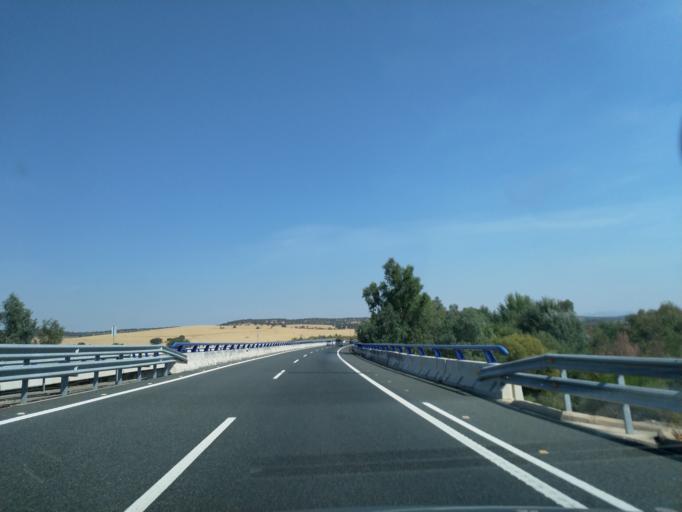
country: ES
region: Extremadura
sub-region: Provincia de Badajoz
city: Aljucen
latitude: 39.0453
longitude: -6.3384
